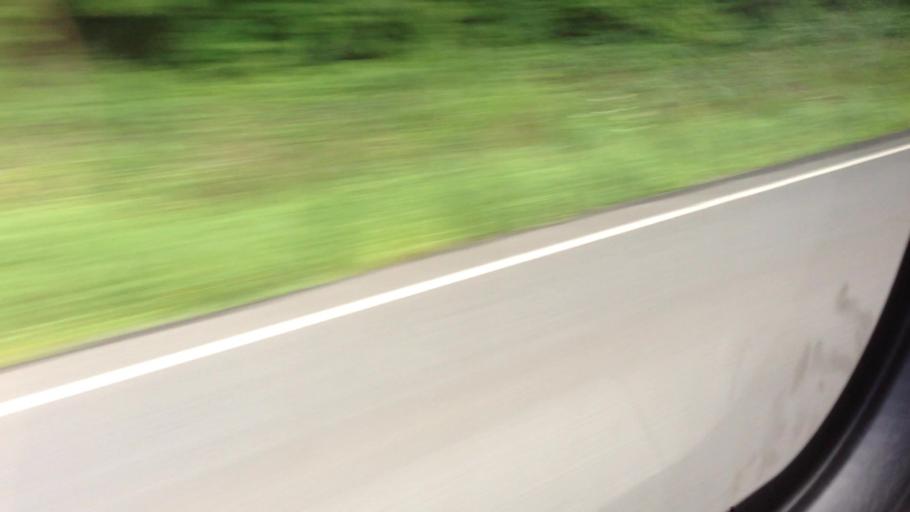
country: US
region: New York
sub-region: Dutchess County
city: Tivoli
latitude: 42.0418
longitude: -73.8948
